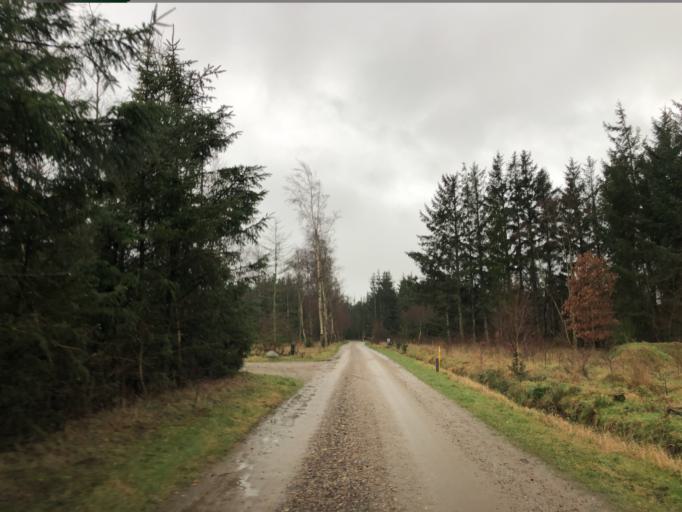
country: DK
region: Central Jutland
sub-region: Holstebro Kommune
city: Ulfborg
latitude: 56.2791
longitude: 8.1620
